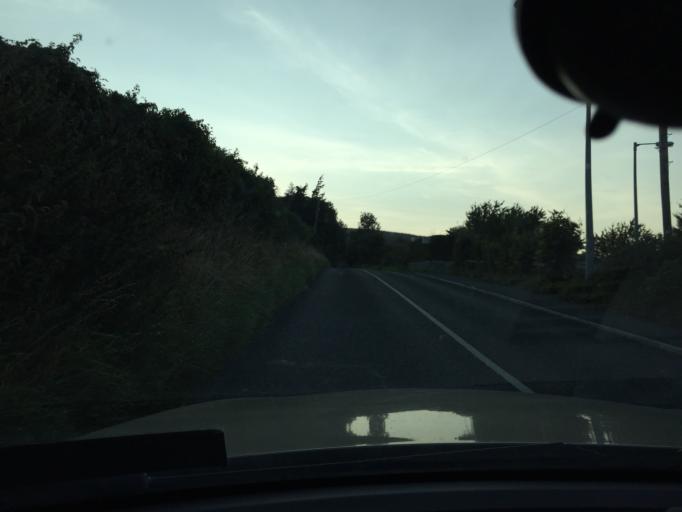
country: IE
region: Leinster
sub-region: Wicklow
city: Enniskerry
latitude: 53.1934
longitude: -6.1865
